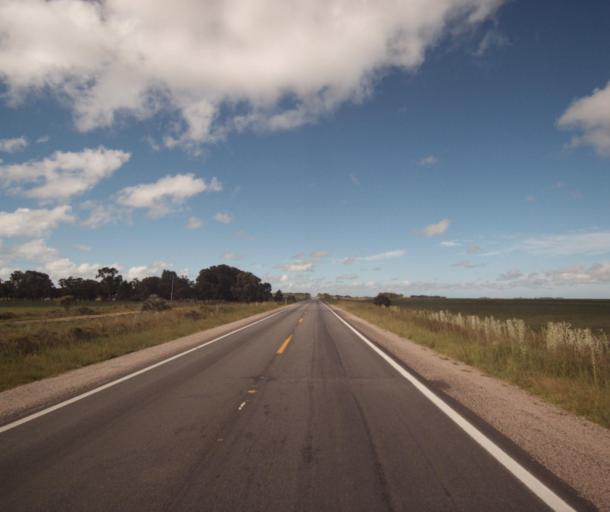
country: UY
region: Cerro Largo
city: Rio Branco
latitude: -32.9480
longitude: -52.7739
